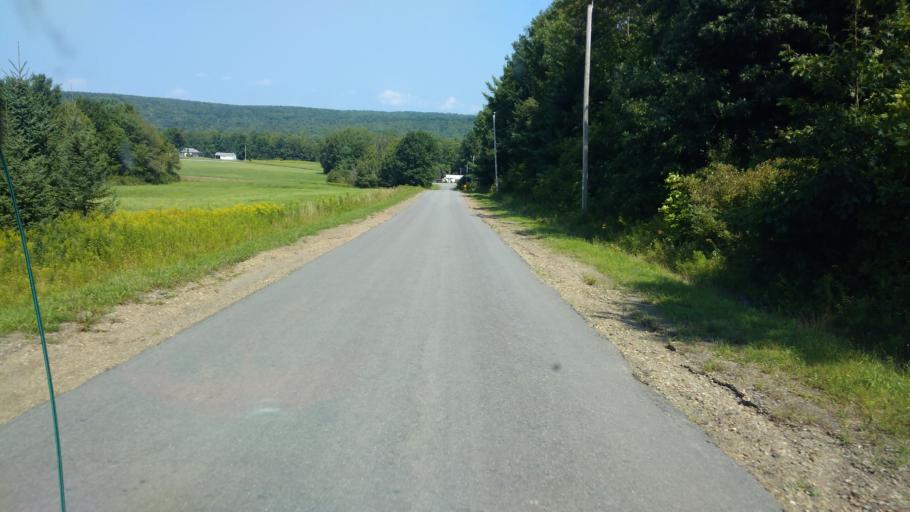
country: US
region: New York
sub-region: Allegany County
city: Houghton
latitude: 42.3387
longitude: -78.0741
